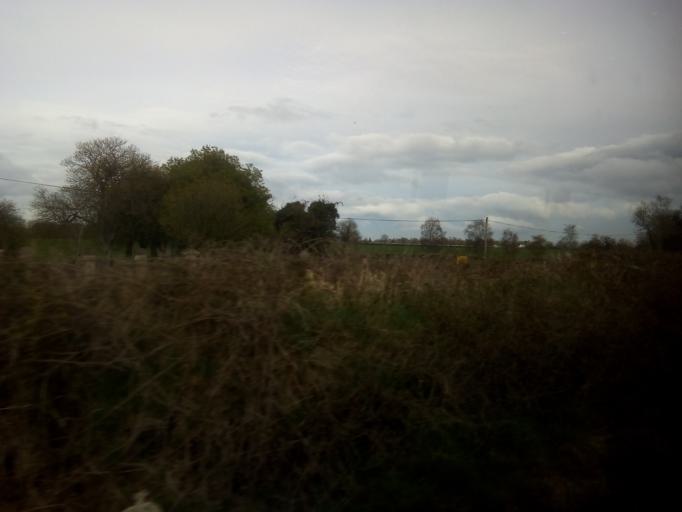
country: IE
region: Leinster
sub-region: Kildare
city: Kilcock
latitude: 53.4207
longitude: -6.7151
